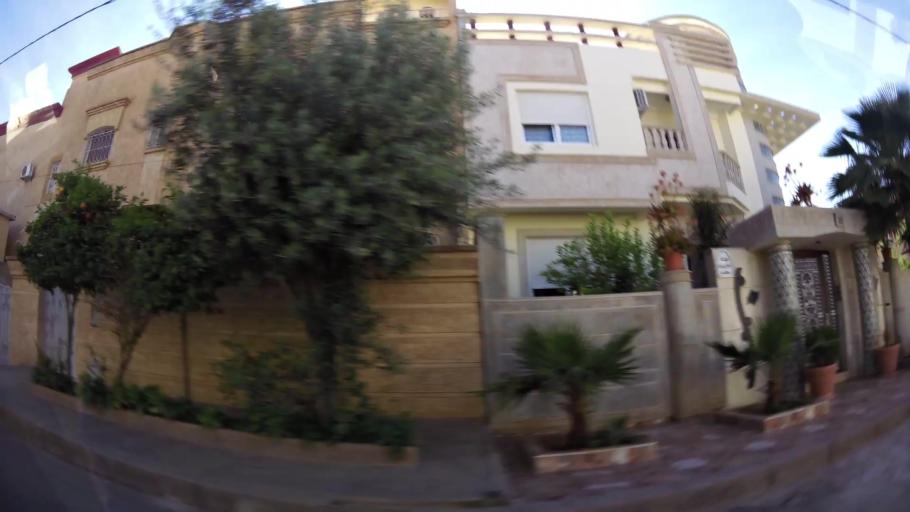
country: MA
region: Oriental
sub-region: Oujda-Angad
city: Oujda
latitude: 34.6655
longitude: -1.9047
